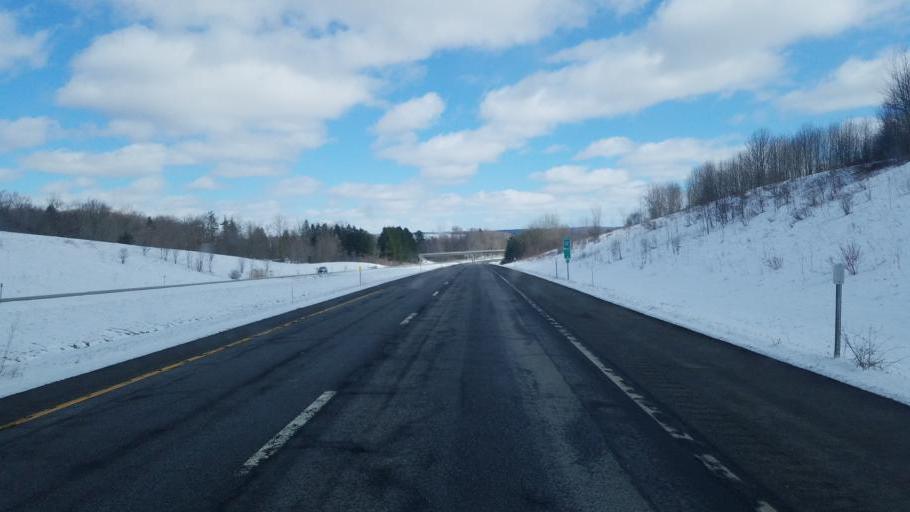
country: US
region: New York
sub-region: Chautauqua County
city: Lakewood
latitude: 42.1532
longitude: -79.4318
